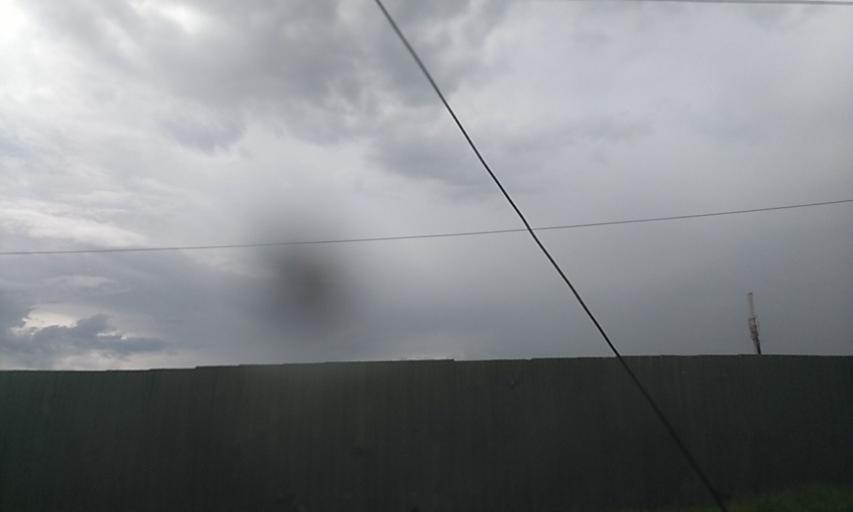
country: UG
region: Central Region
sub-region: Kampala District
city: Kampala
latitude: 0.3276
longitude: 32.5929
